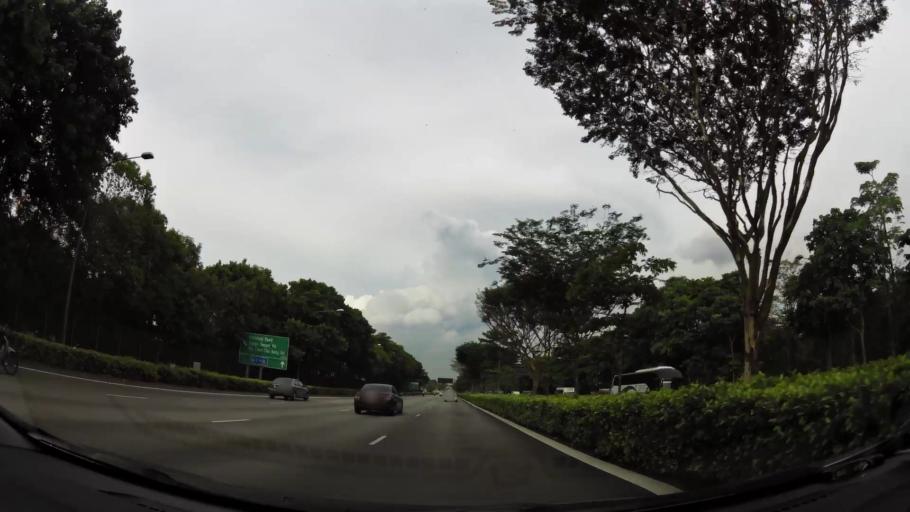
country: MY
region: Johor
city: Johor Bahru
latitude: 1.3728
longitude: 103.7254
